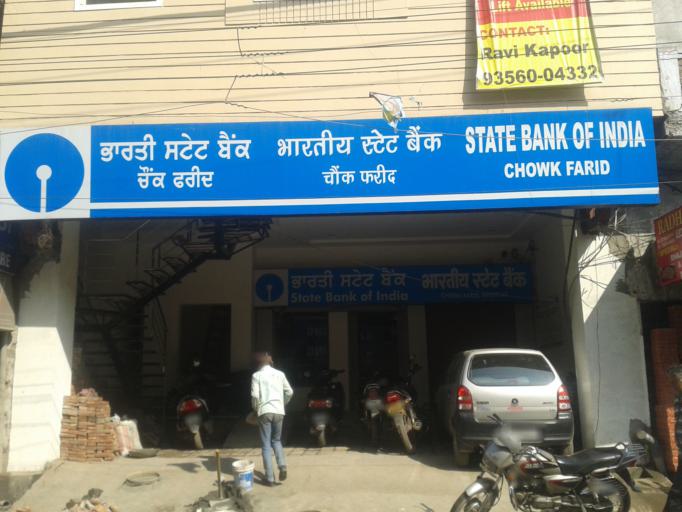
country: IN
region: Punjab
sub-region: Amritsar
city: Amritsar
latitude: 31.6272
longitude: 74.8756
